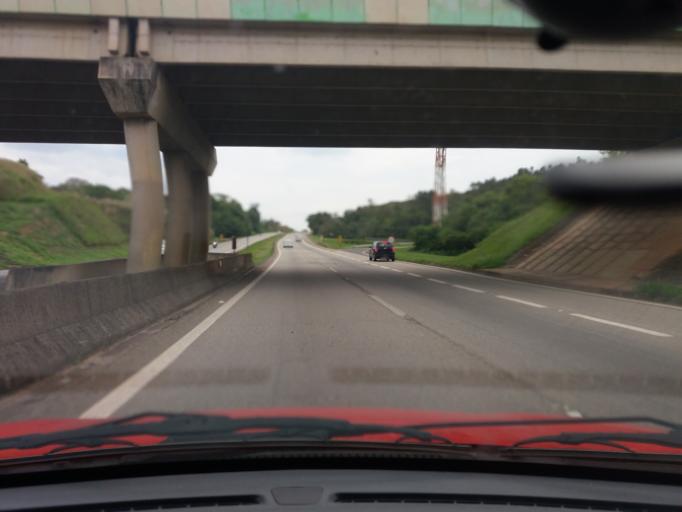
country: BR
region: Sao Paulo
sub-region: Itupeva
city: Itupeva
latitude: -23.1959
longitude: -46.9949
